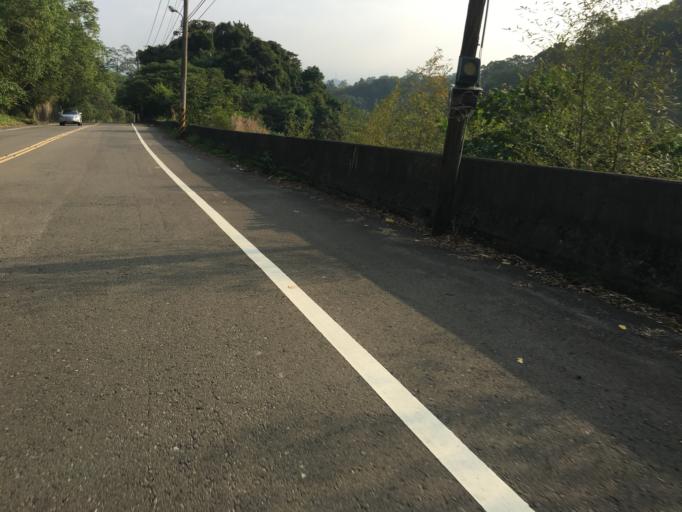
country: TW
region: Taiwan
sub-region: Hsinchu
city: Hsinchu
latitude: 24.7122
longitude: 121.0430
